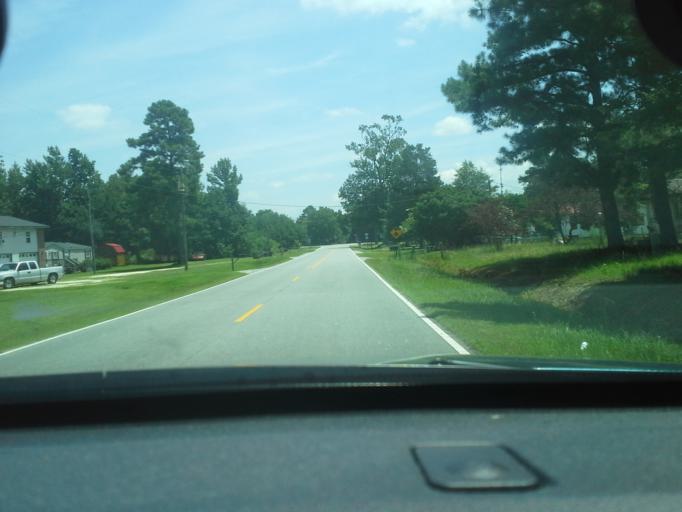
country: US
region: North Carolina
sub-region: Chowan County
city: Edenton
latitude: 35.9251
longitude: -76.5932
